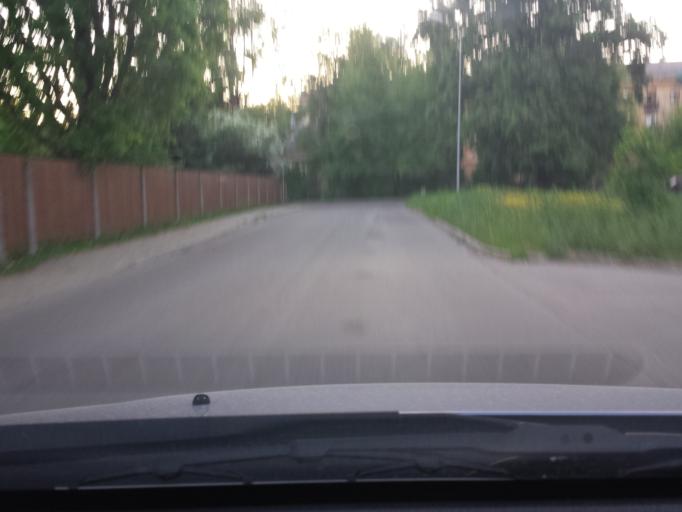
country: LV
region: Riga
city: Jaunciems
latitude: 56.9809
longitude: 24.1964
